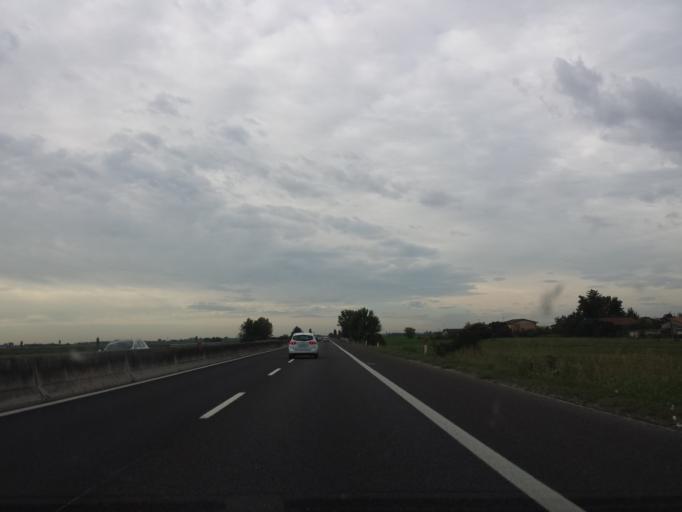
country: IT
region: Veneto
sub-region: Provincia di Padova
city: Pozzonovo
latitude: 45.1822
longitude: 11.7763
